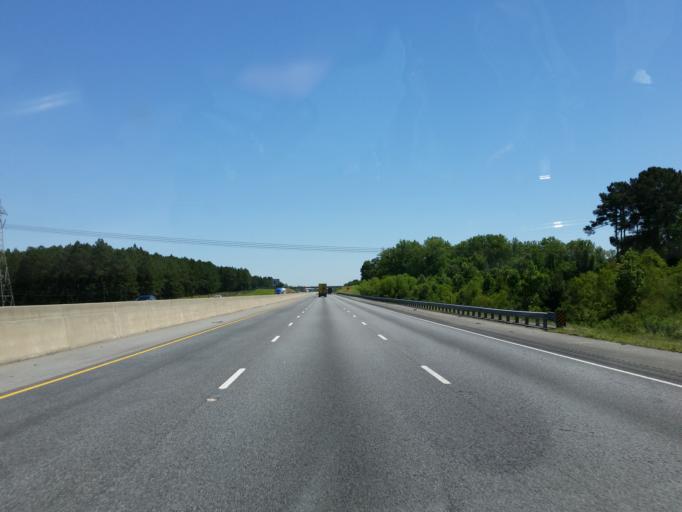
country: US
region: Georgia
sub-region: Tift County
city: Tifton
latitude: 31.5389
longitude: -83.5284
